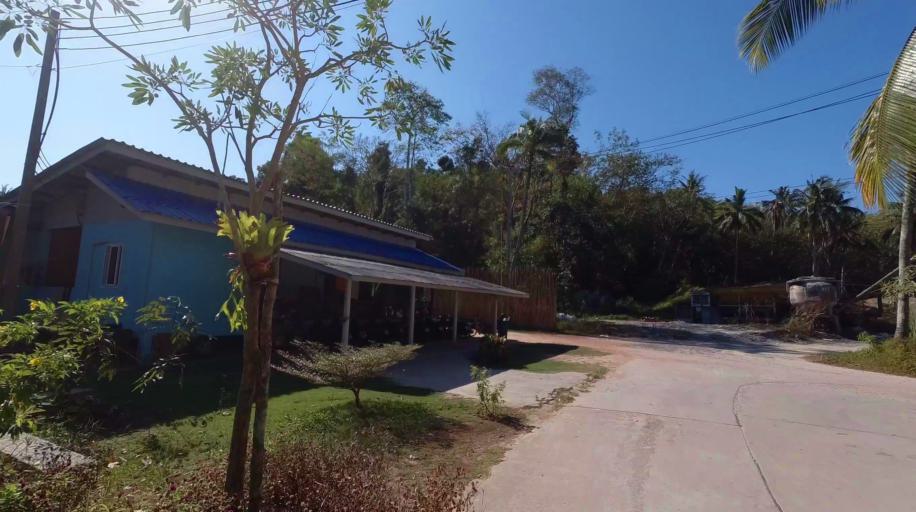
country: TH
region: Trat
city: Ko Kut
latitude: 11.6204
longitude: 102.5503
